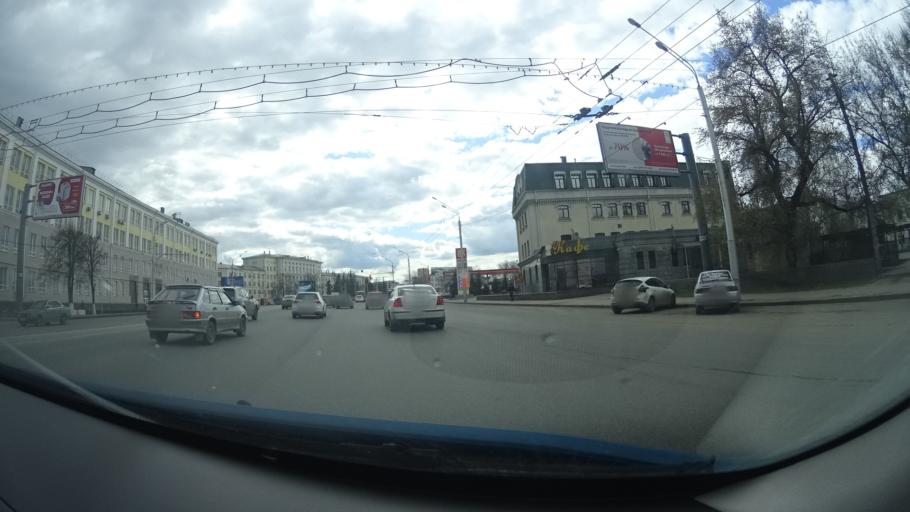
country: RU
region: Bashkortostan
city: Ufa
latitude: 54.7407
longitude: 55.9857
